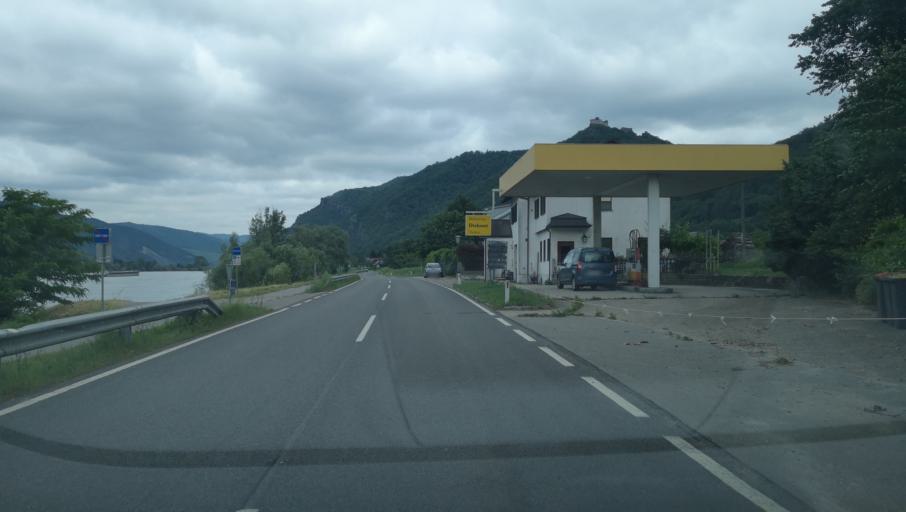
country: AT
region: Lower Austria
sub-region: Politischer Bezirk Krems
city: Aggsbach
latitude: 48.3013
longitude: 15.4108
